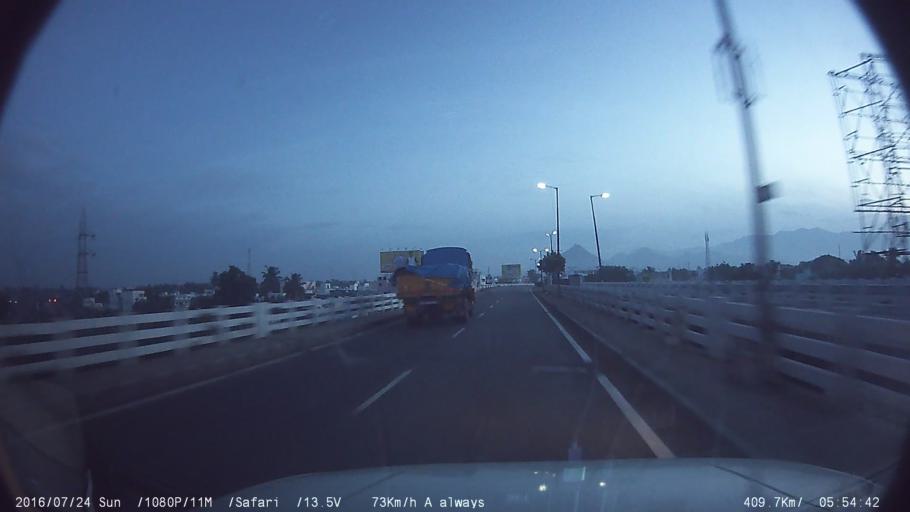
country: IN
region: Tamil Nadu
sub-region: Salem
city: Salem
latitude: 11.6595
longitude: 78.1216
